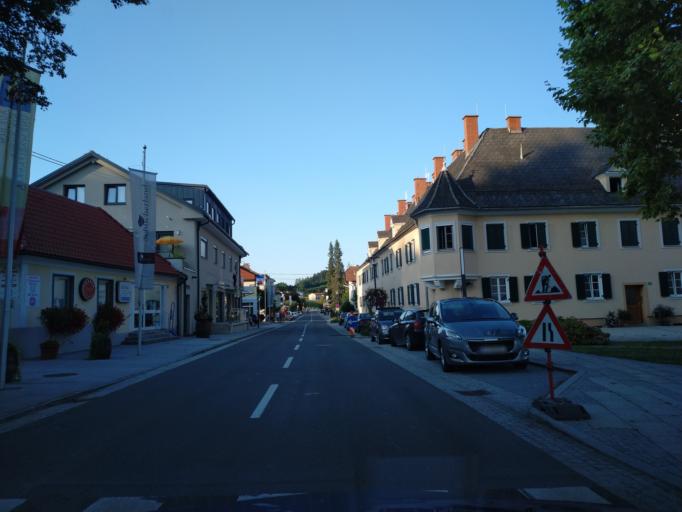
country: AT
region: Styria
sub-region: Politischer Bezirk Deutschlandsberg
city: Wies
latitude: 46.7190
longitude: 15.2711
